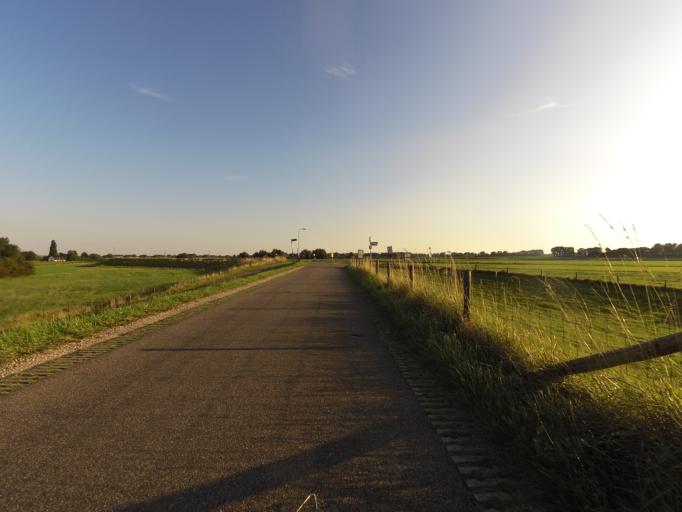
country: NL
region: Gelderland
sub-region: Gemeente Westervoort
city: Westervoort
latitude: 51.9363
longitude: 5.9688
